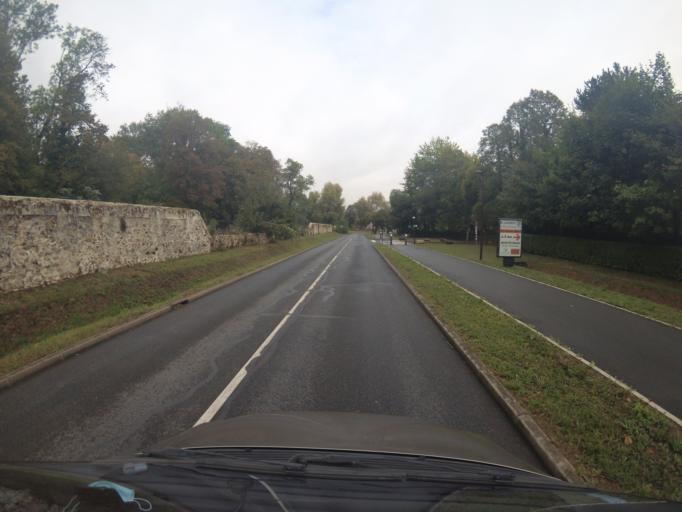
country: FR
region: Ile-de-France
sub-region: Departement de Seine-et-Marne
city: Guermantes
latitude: 48.8523
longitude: 2.7039
